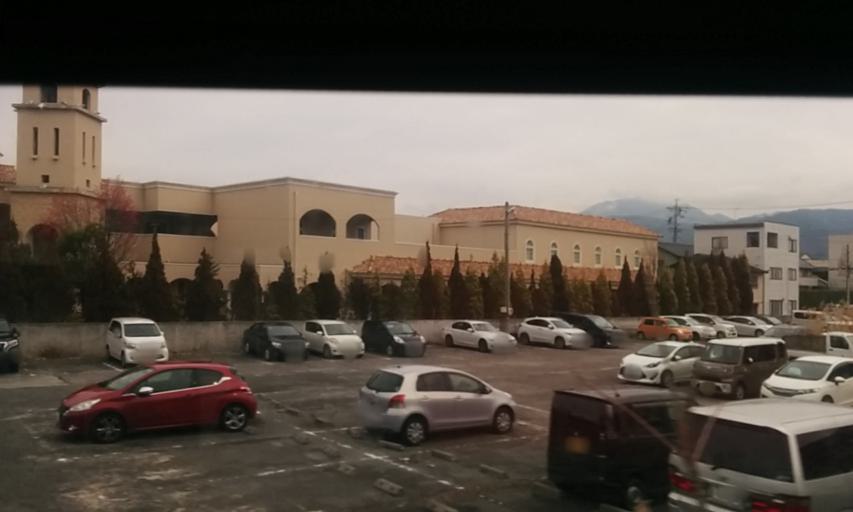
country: JP
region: Nagano
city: Matsumoto
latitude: 36.2388
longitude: 137.9599
